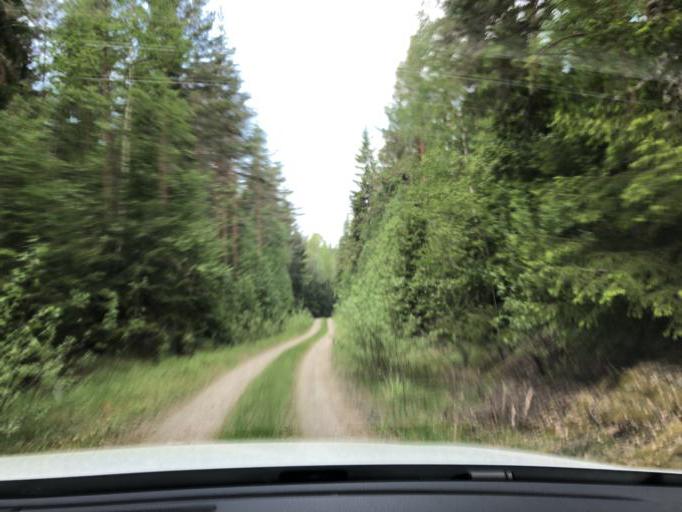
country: SE
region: Dalarna
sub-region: Avesta Kommun
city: Horndal
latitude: 60.2166
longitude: 16.5013
